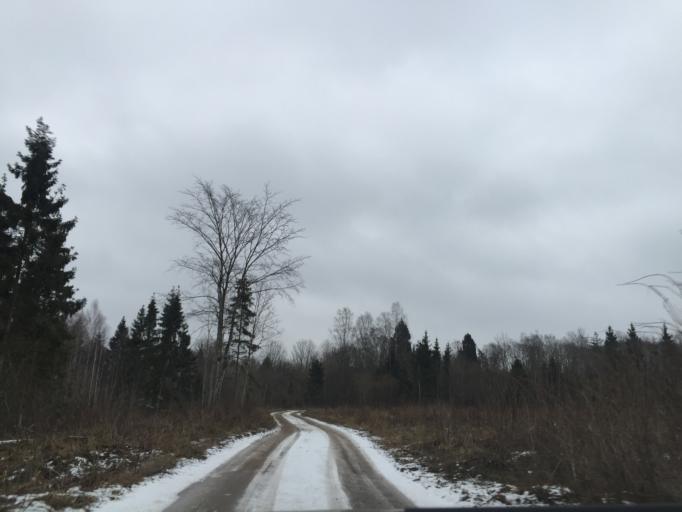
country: EE
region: Saare
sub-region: Kuressaare linn
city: Kuressaare
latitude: 58.3805
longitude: 22.2405
